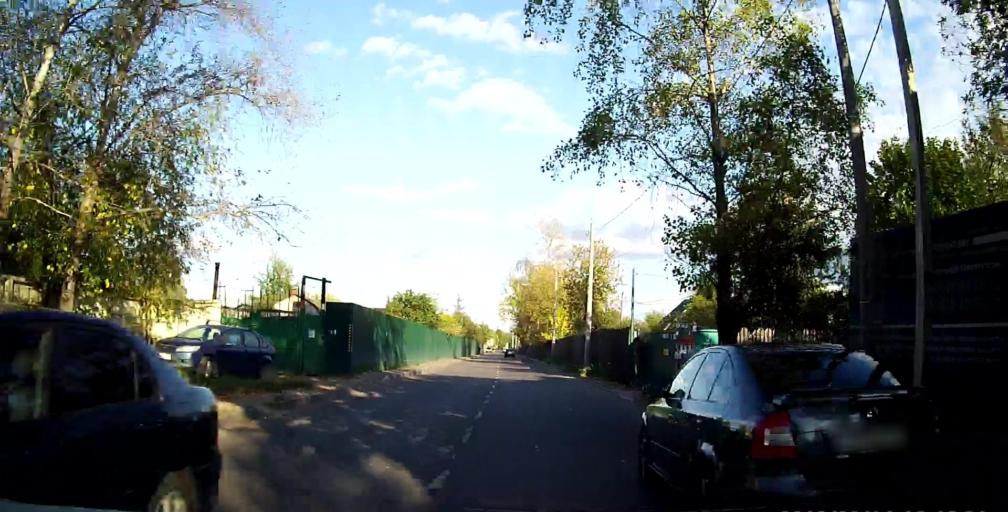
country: RU
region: Moskovskaya
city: Klimovsk
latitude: 55.3680
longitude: 37.5402
